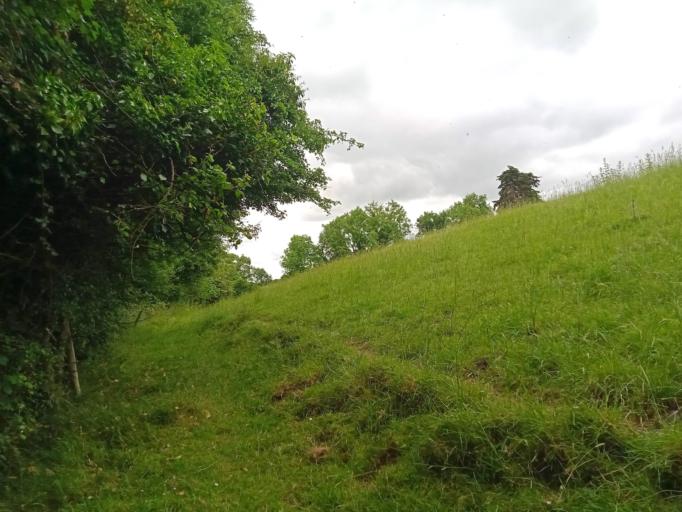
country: IE
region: Leinster
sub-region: Kilkenny
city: Ballyragget
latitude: 52.7779
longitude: -7.4664
